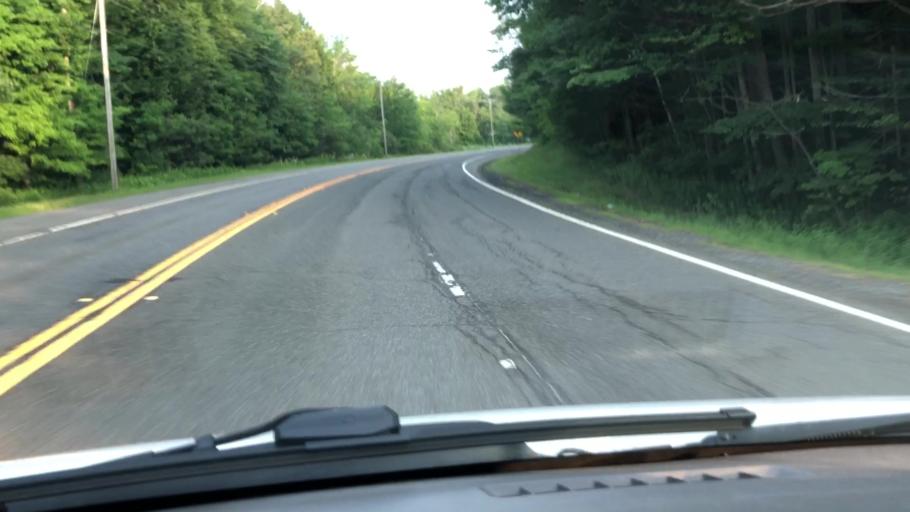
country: US
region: Massachusetts
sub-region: Berkshire County
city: Hinsdale
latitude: 42.4829
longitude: -72.9849
